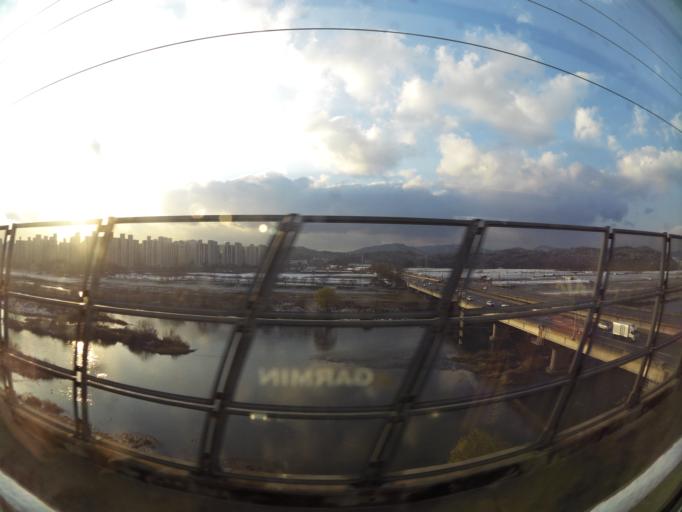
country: KR
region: Daejeon
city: Songgang-dong
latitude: 36.4040
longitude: 127.4148
